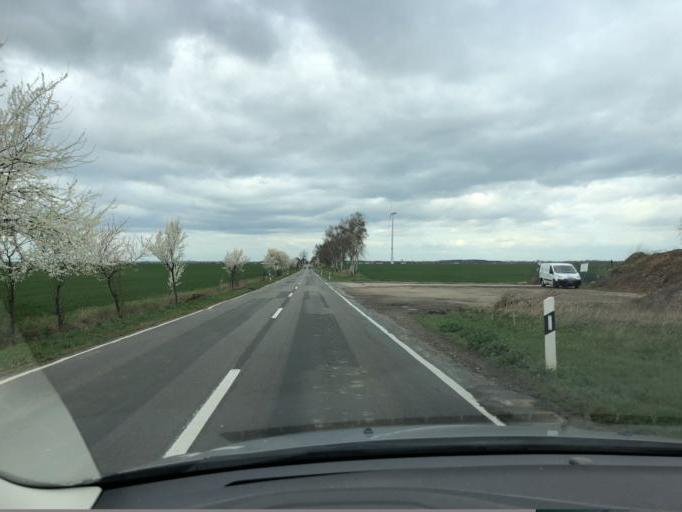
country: DE
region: Saxony-Anhalt
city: Muschwitz
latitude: 51.2217
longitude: 12.1401
